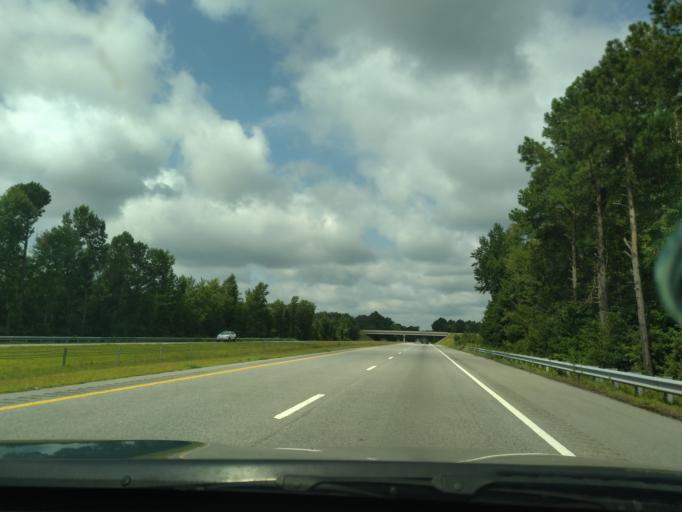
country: US
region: North Carolina
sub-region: Martin County
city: Williamston
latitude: 35.8266
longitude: -77.1500
